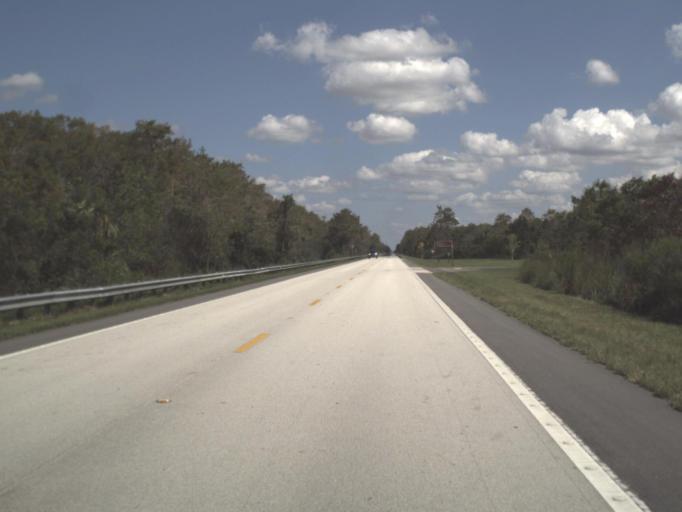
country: US
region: Florida
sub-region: Miami-Dade County
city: Kendall West
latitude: 25.8525
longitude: -80.9907
